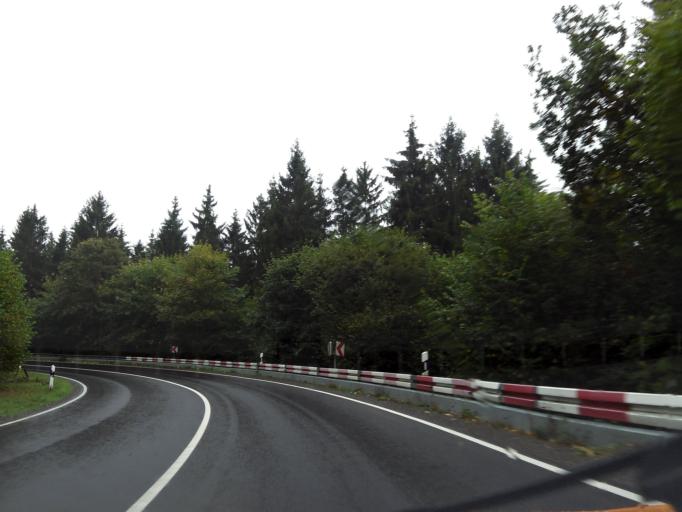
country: DE
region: Saxony-Anhalt
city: Friedrichsbrunn
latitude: 51.6499
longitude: 11.0714
